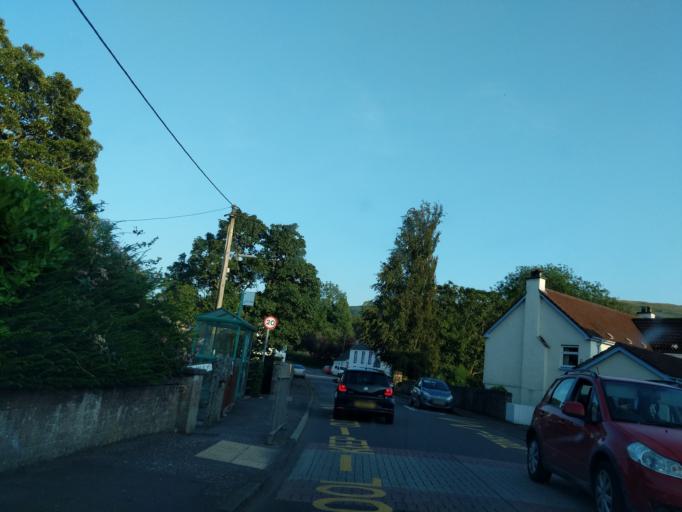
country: GB
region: Scotland
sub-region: Stirling
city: Doune
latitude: 56.1251
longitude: -4.0834
